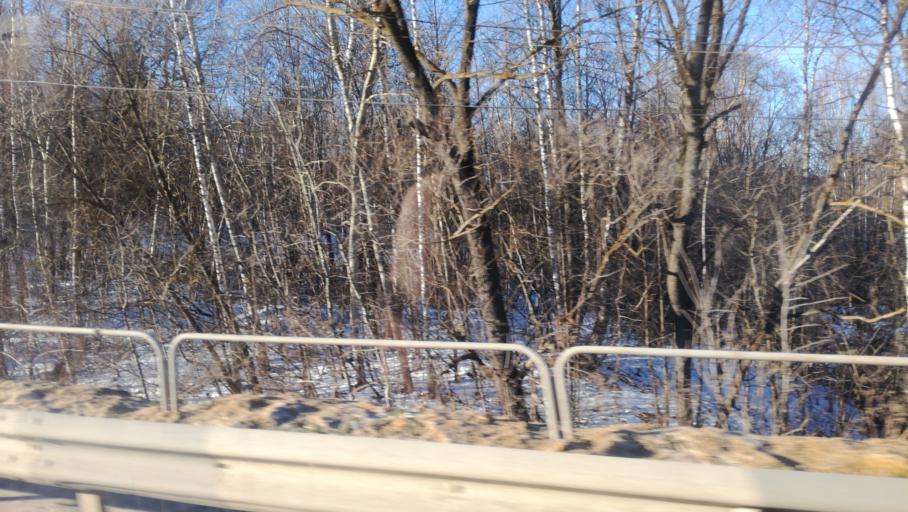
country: RU
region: Tula
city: Kosaya Gora
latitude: 54.1685
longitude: 37.4705
